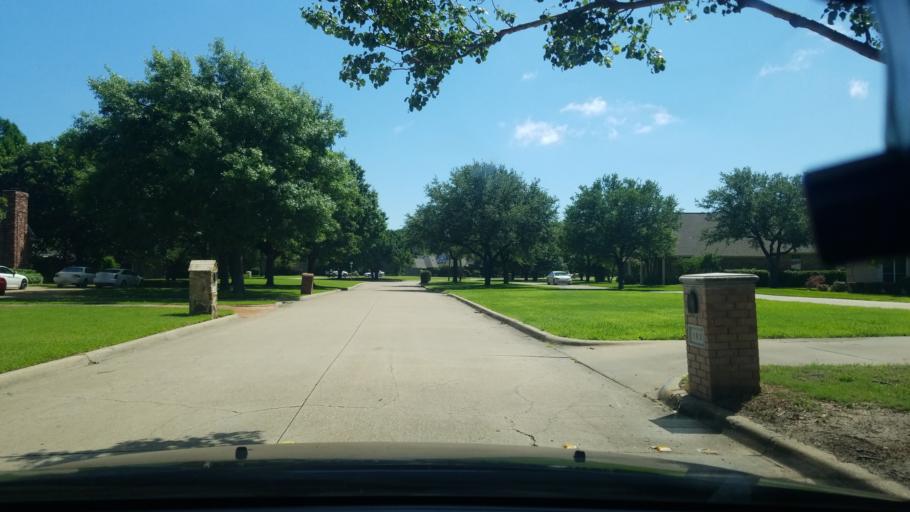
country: US
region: Texas
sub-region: Dallas County
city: Mesquite
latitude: 32.7977
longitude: -96.5933
